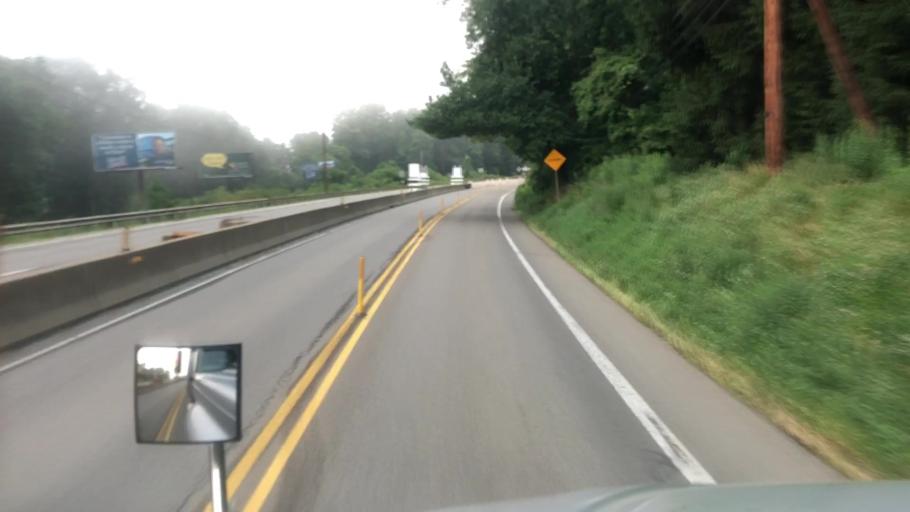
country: US
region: Pennsylvania
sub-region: Venango County
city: Woodland Heights
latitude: 41.4082
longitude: -79.7374
